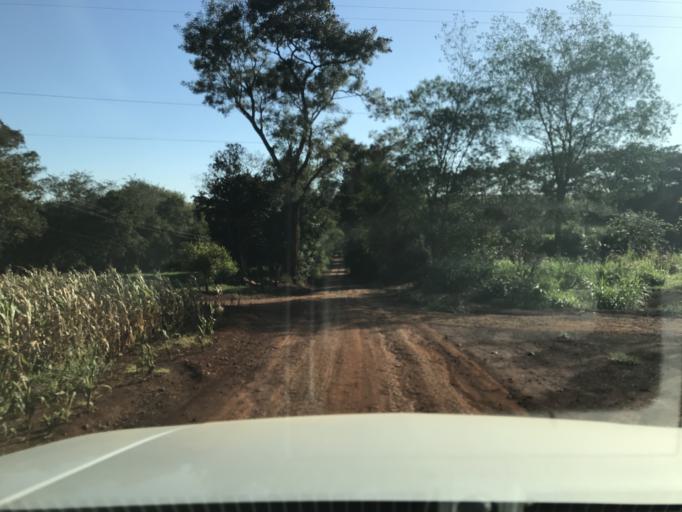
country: BR
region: Parana
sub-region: Palotina
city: Palotina
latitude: -24.2273
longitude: -53.8130
